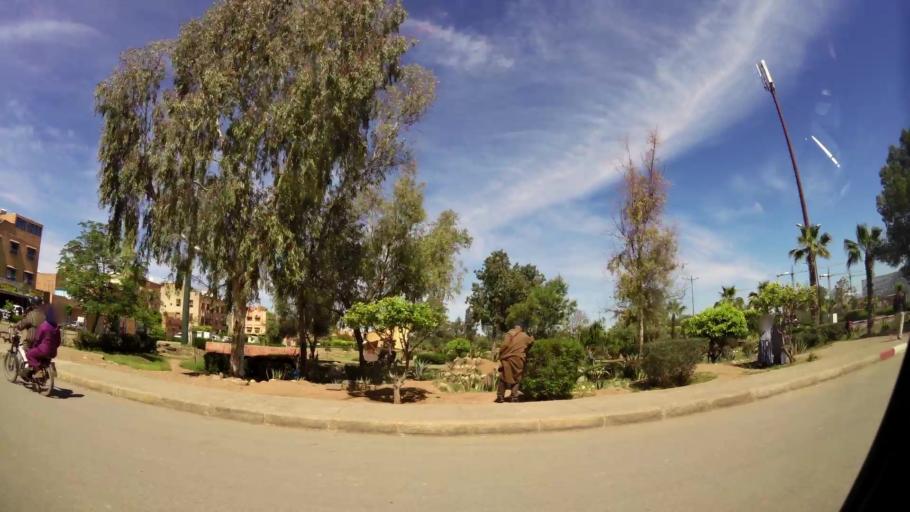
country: MA
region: Marrakech-Tensift-Al Haouz
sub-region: Marrakech
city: Marrakesh
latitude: 31.6035
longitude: -7.9618
